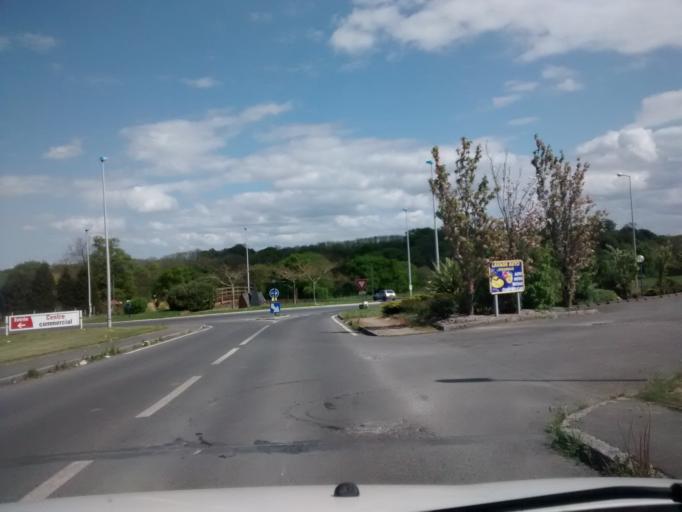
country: FR
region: Brittany
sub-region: Departement des Cotes-d'Armor
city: Lanvallay
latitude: 48.4711
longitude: -2.0448
